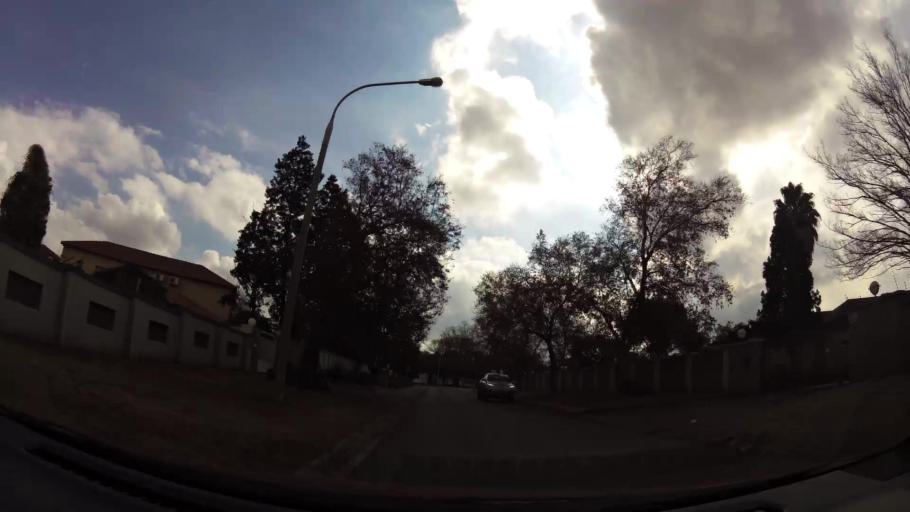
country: ZA
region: Gauteng
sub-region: Sedibeng District Municipality
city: Vanderbijlpark
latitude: -26.7399
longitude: 27.8271
